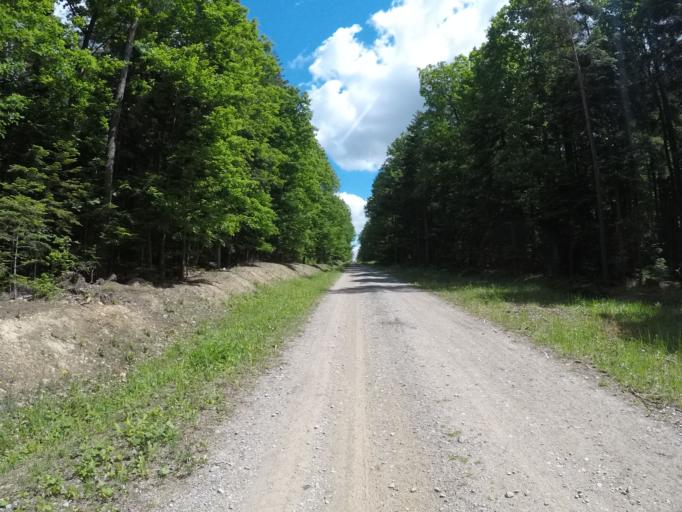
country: PL
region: Swietokrzyskie
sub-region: Powiat kielecki
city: Kostomloty Pierwsze
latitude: 50.9347
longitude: 20.6138
